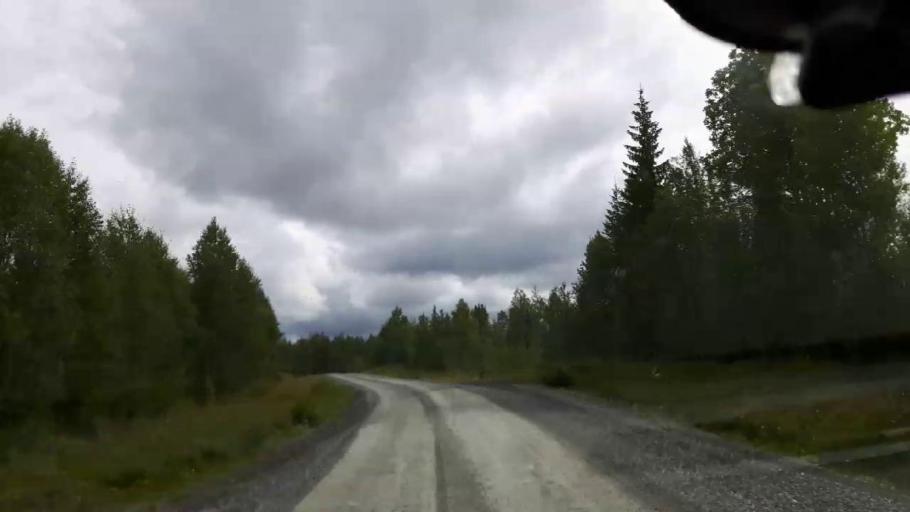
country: SE
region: Jaemtland
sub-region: Krokoms Kommun
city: Valla
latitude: 63.6046
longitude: 14.1289
